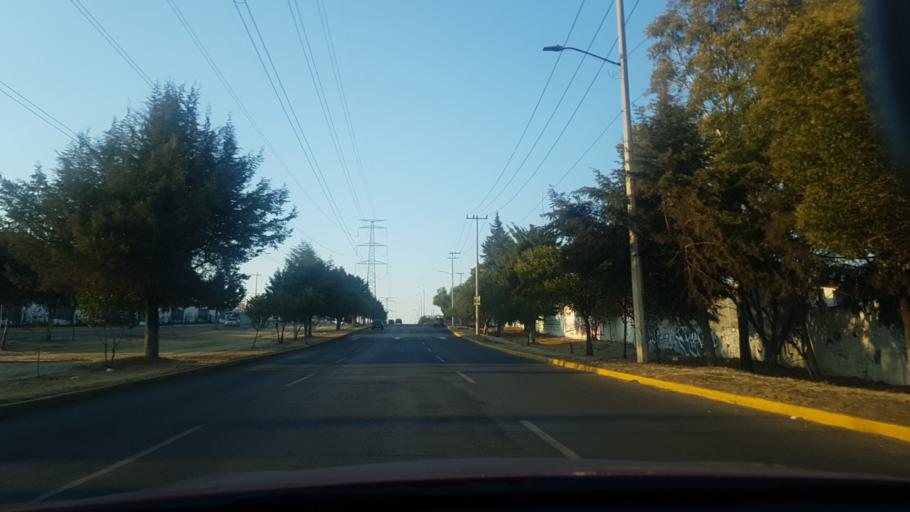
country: MX
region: Mexico
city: Cuautitlan Izcalli
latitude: 19.6375
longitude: -99.2208
